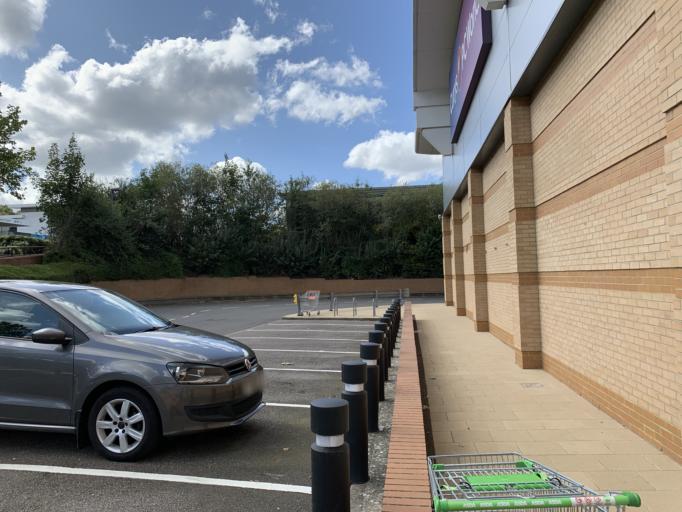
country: GB
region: England
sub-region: Kent
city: Pembury
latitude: 51.1573
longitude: 0.2933
